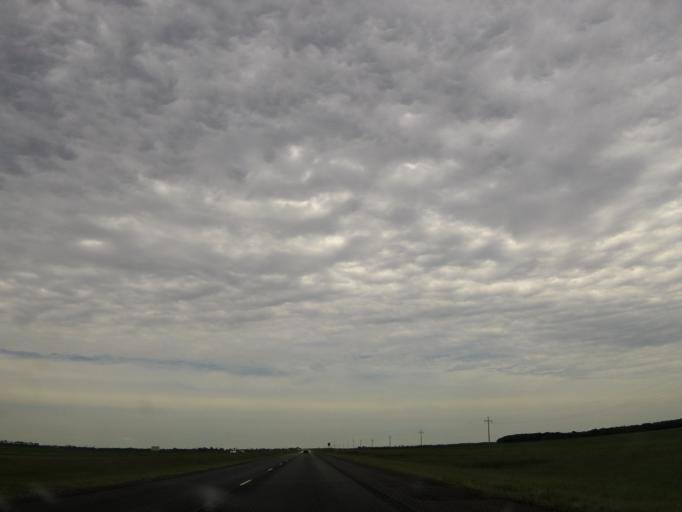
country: US
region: North Dakota
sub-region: Walsh County
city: Grafton
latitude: 48.2445
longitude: -97.1891
